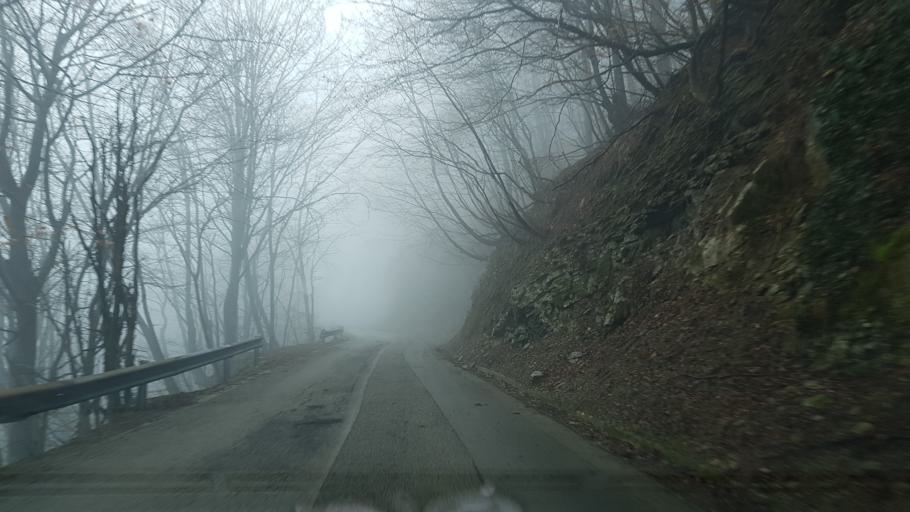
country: IT
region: Friuli Venezia Giulia
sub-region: Provincia di Udine
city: Cras
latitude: 46.1522
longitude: 13.6219
